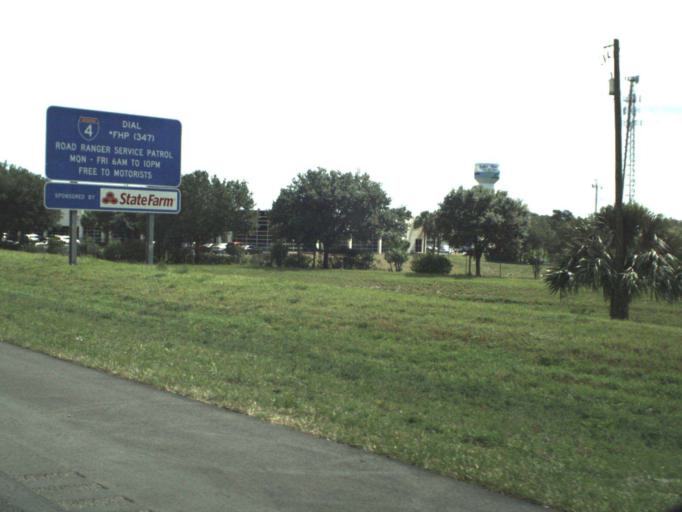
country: US
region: Florida
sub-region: Seminole County
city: Heathrow
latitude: 28.7327
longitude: -81.3714
